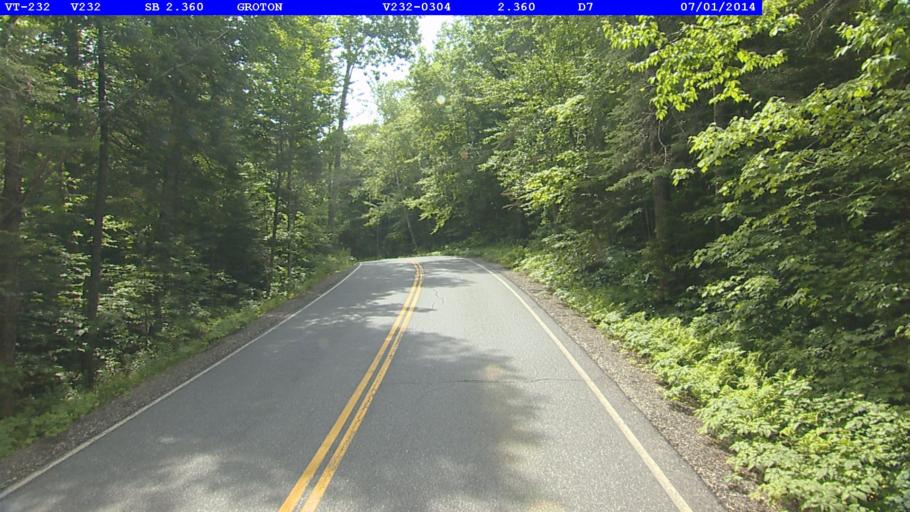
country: US
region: New Hampshire
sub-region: Grafton County
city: Woodsville
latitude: 44.2443
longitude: -72.2516
